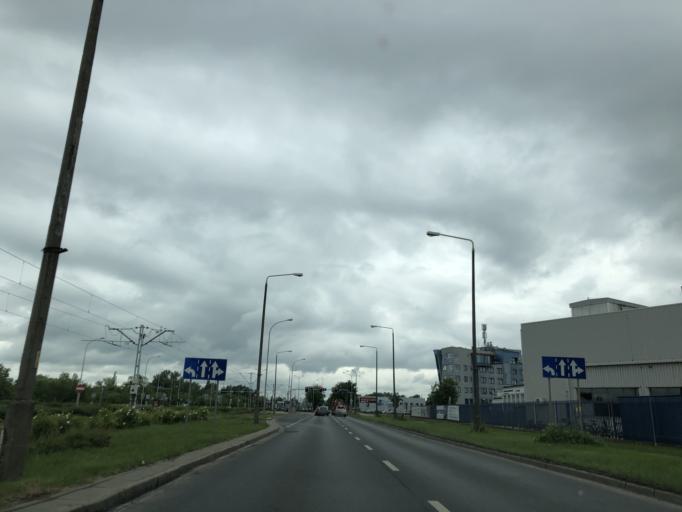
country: PL
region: Lower Silesian Voivodeship
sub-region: Powiat trzebnicki
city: Psary
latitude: 51.1462
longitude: 17.0307
